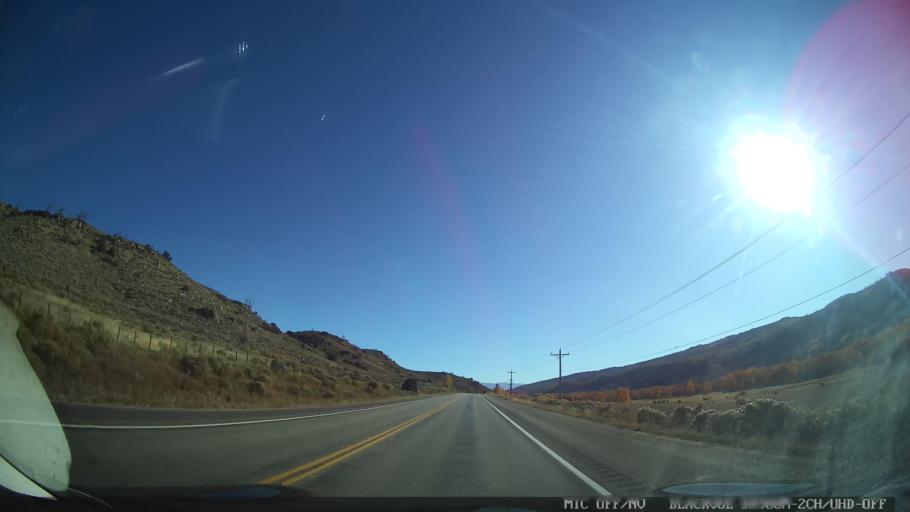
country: US
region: Colorado
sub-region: Grand County
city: Hot Sulphur Springs
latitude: 40.0976
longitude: -106.0518
